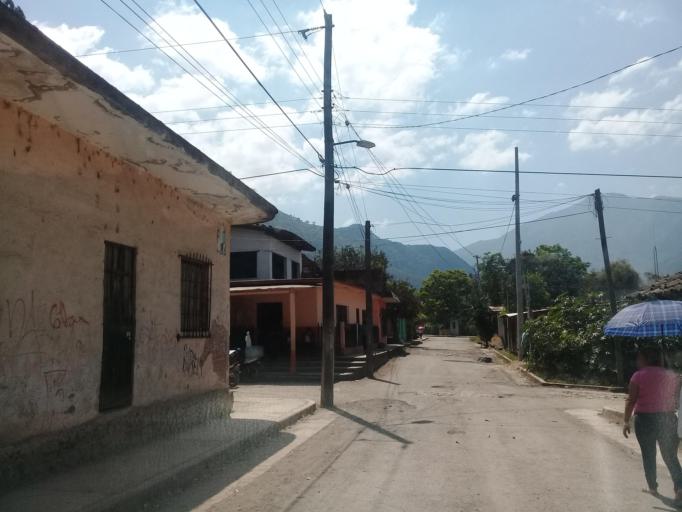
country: MX
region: Veracruz
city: Jalapilla
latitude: 18.8104
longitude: -97.0696
